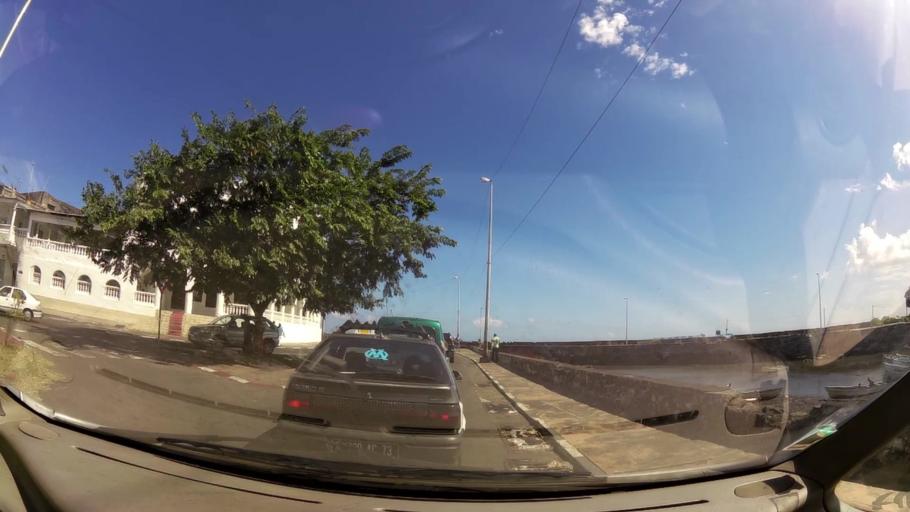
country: KM
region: Grande Comore
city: Moroni
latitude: -11.7036
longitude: 43.2520
